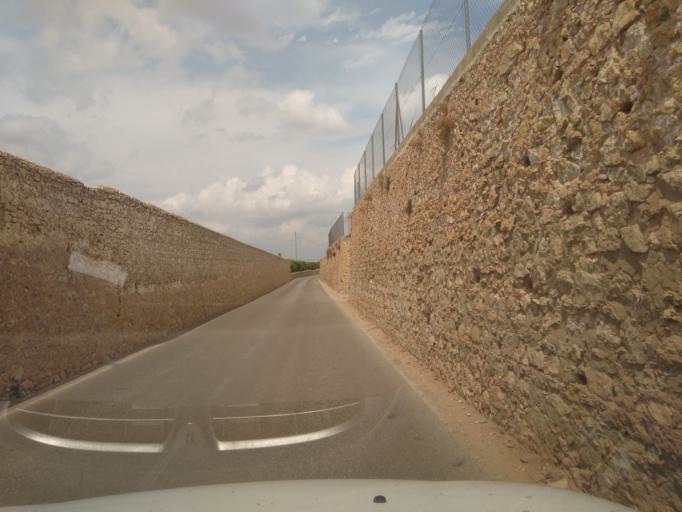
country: ES
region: Valencia
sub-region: Provincia de Valencia
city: Carcaixent
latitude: 39.1047
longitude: -0.4341
